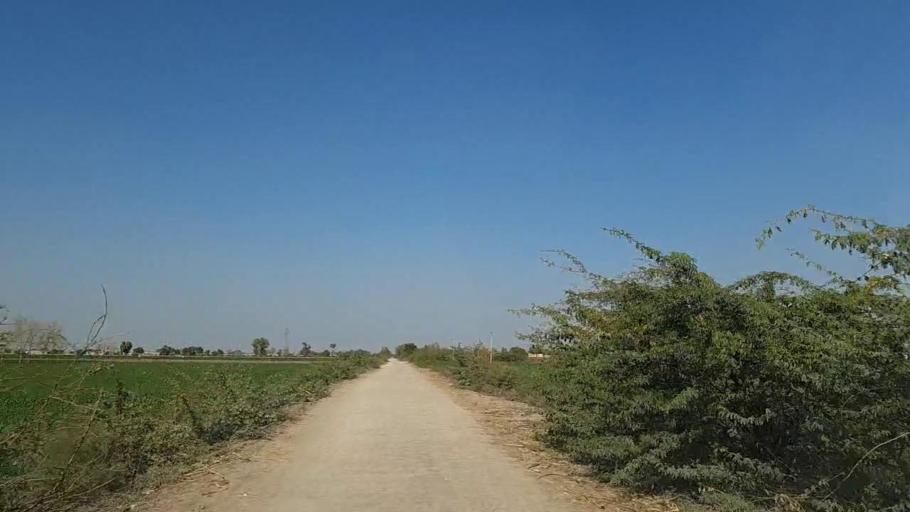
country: PK
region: Sindh
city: Nawabshah
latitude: 26.2472
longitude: 68.4410
